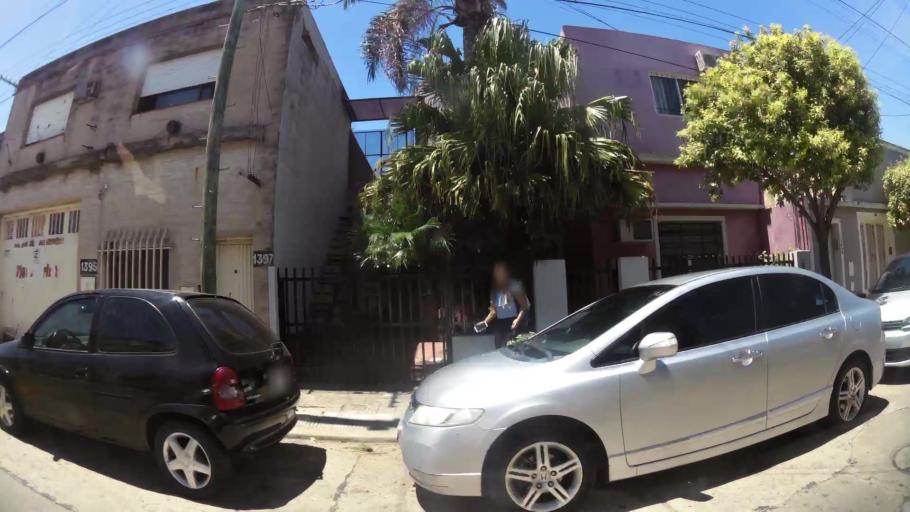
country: AR
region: Santa Fe
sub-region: Departamento de Rosario
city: Rosario
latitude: -32.9441
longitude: -60.6957
